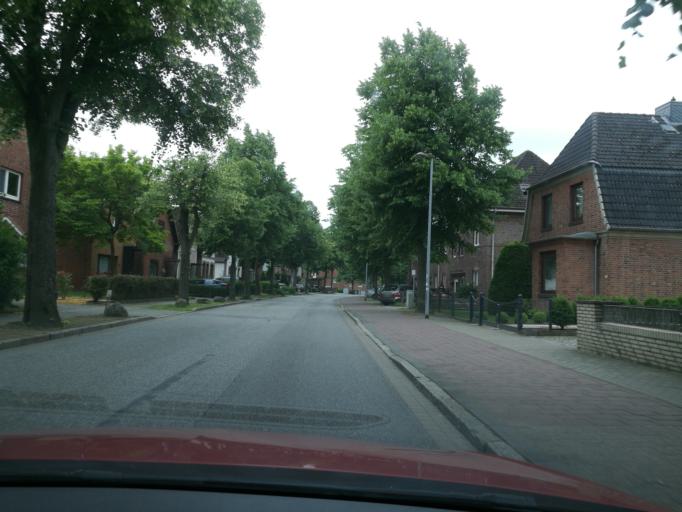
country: DE
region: Schleswig-Holstein
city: Bad Oldesloe
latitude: 53.8011
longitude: 10.3839
